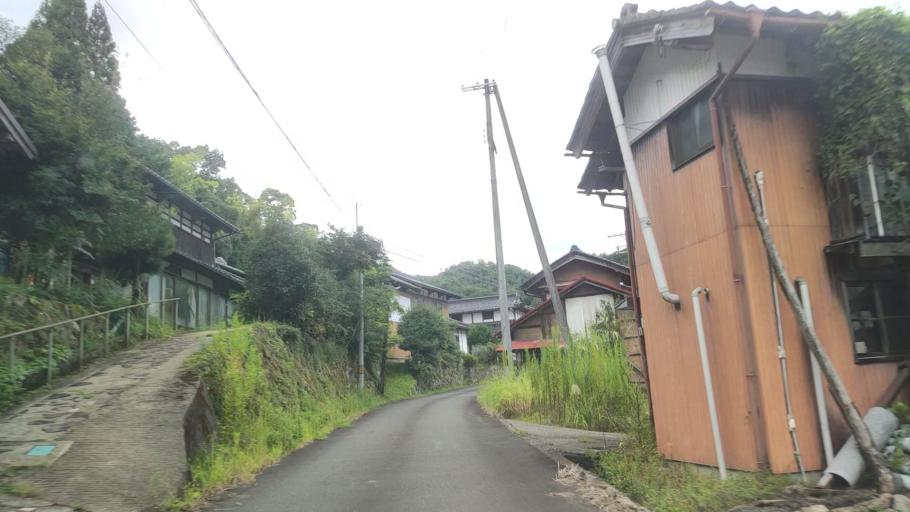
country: JP
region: Hyogo
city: Toyooka
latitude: 35.6000
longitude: 134.8804
